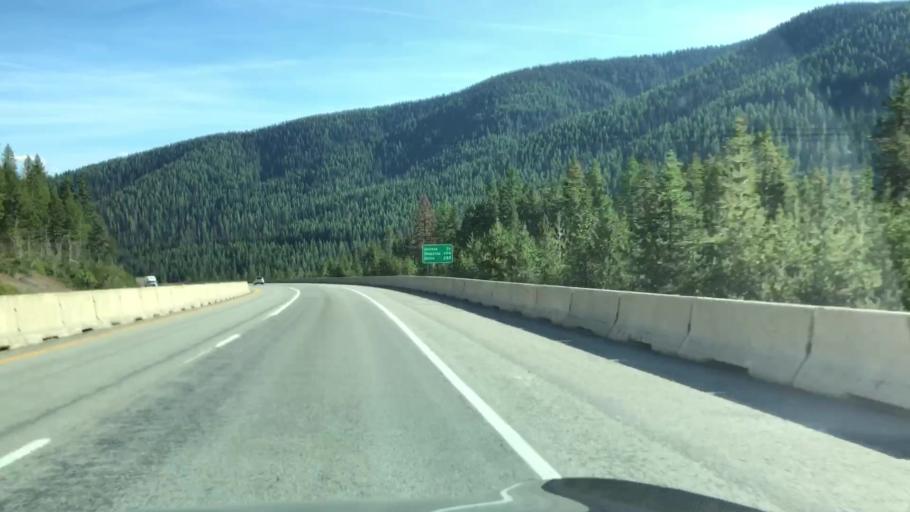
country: US
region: Idaho
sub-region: Shoshone County
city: Wallace
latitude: 47.4442
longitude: -115.6914
